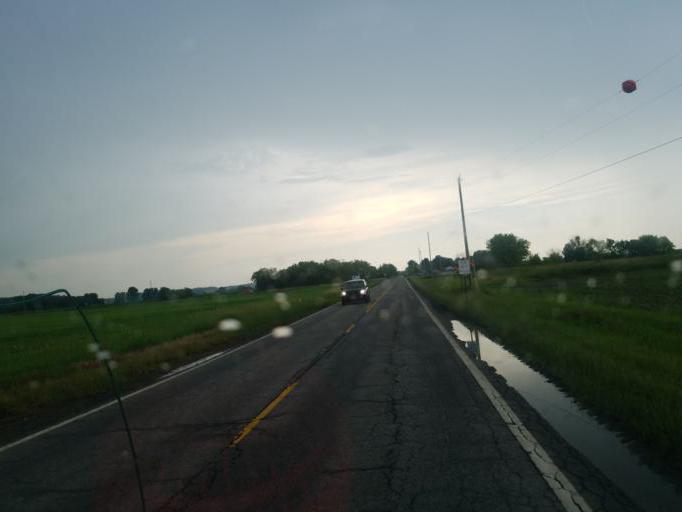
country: US
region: Ohio
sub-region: Wayne County
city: Rittman
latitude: 40.9458
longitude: -81.8094
